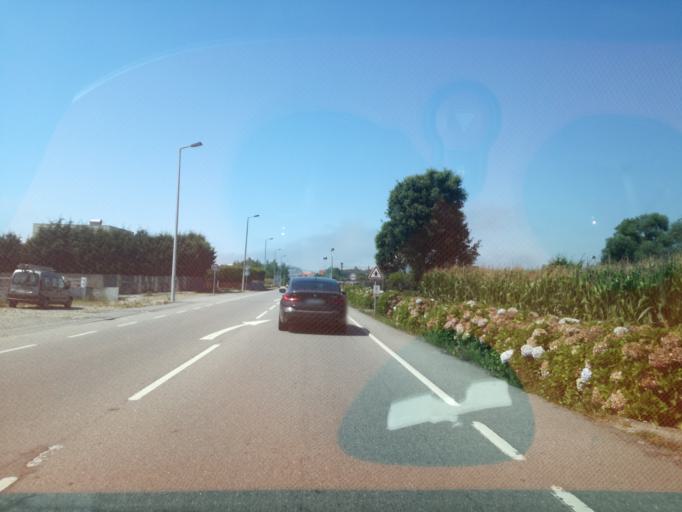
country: PT
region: Braga
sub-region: Esposende
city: Apulia
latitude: 41.5077
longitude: -8.7656
